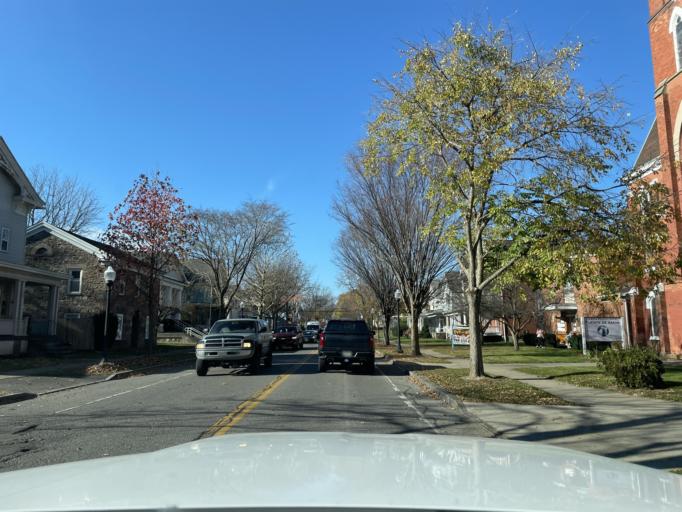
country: US
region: New York
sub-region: Orleans County
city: Medina
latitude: 43.2204
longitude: -78.3900
